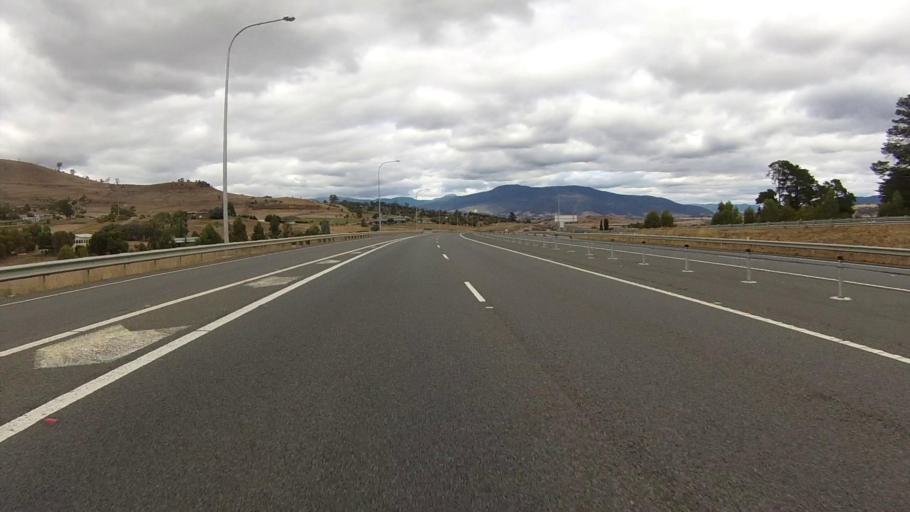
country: AU
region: Tasmania
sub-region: Brighton
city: Bridgewater
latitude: -42.6981
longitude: 147.2765
